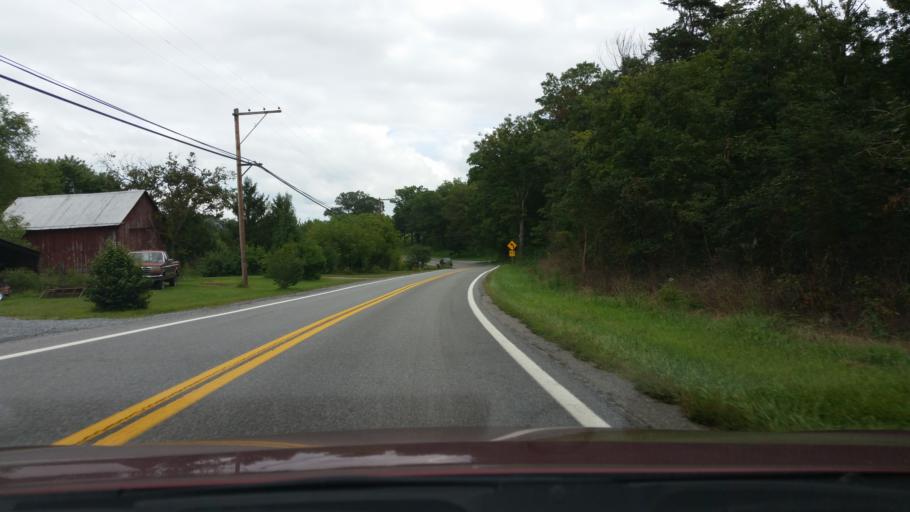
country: US
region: West Virginia
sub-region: Morgan County
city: Berkeley Springs
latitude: 39.6338
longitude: -78.1650
